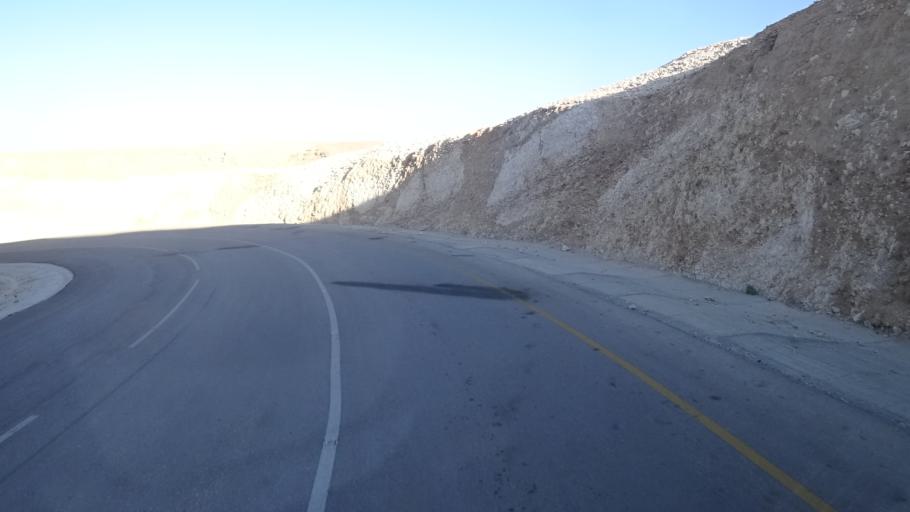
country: YE
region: Al Mahrah
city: Hawf
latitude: 17.0915
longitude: 53.0417
